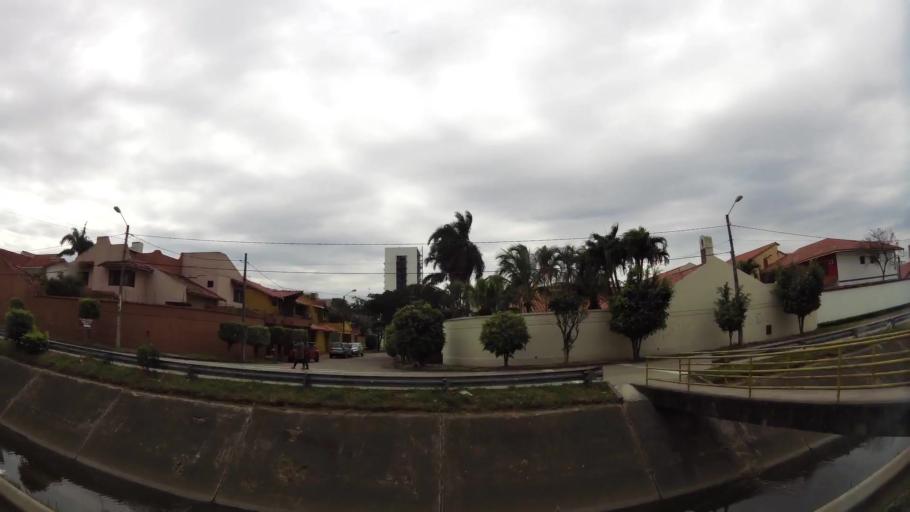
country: BO
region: Santa Cruz
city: Santa Cruz de la Sierra
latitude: -17.7670
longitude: -63.2043
